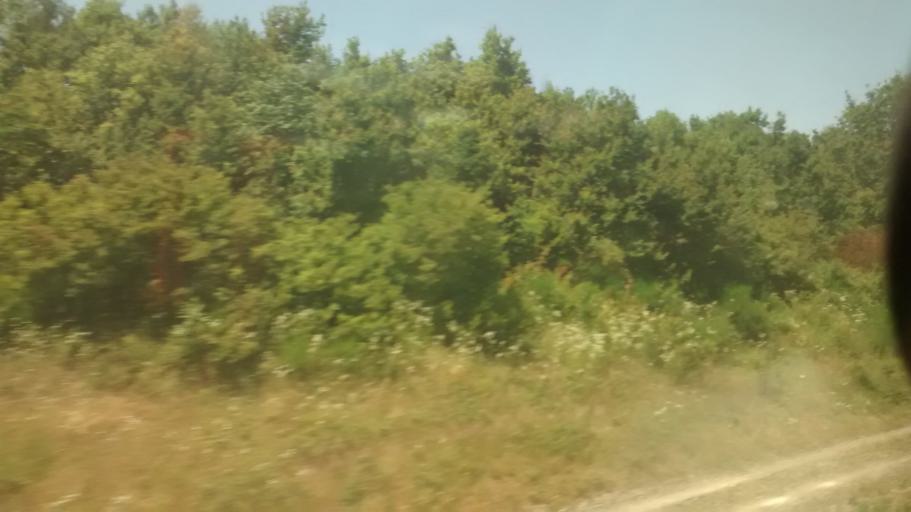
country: FR
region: Rhone-Alpes
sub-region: Departement du Rhone
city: Pusignan
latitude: 45.7444
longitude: 5.0793
